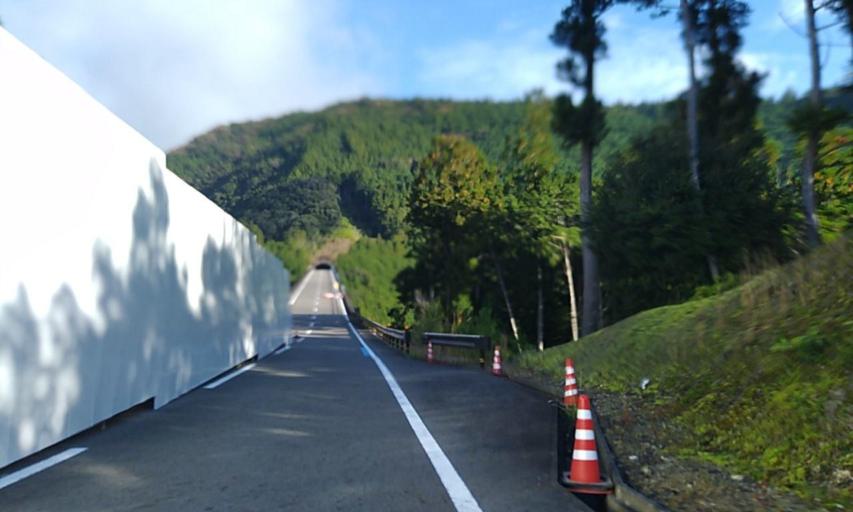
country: JP
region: Wakayama
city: Shingu
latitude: 33.8923
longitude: 135.8798
